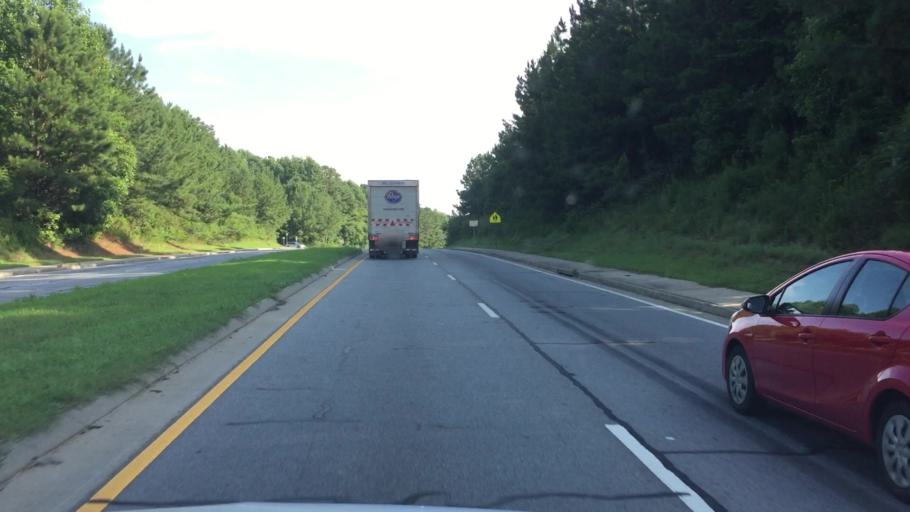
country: US
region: Georgia
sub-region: Rockdale County
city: Lakeview Estates
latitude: 33.7785
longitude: -84.0474
